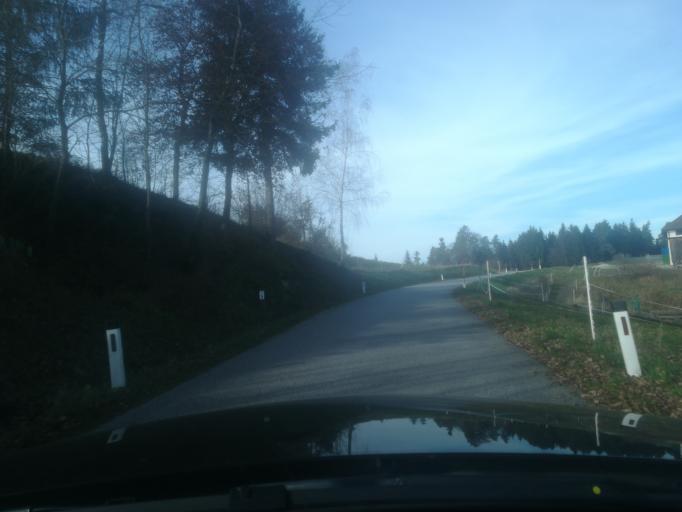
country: AT
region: Upper Austria
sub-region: Politischer Bezirk Perg
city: Perg
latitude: 48.3263
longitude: 14.6541
